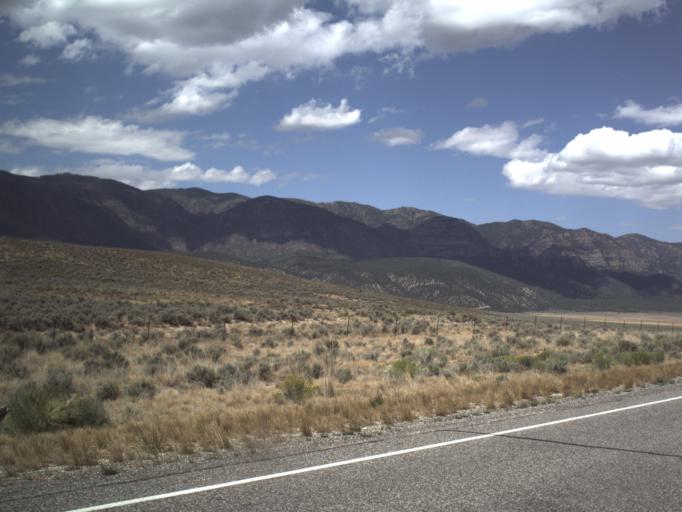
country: US
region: Utah
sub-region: Sevier County
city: Aurora
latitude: 39.0231
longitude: -112.0355
